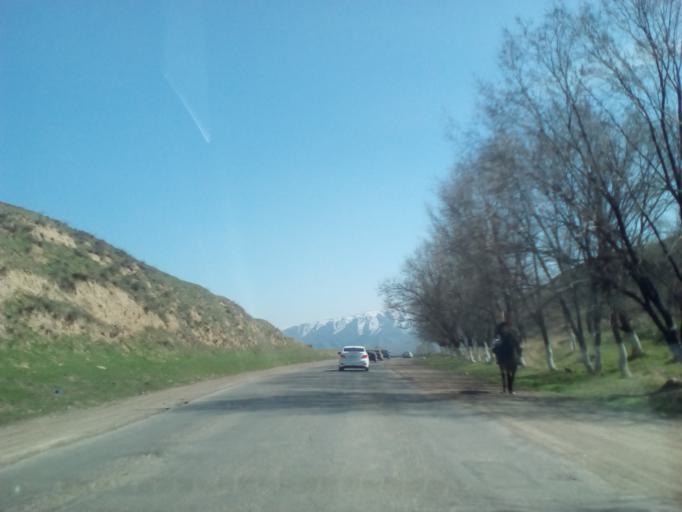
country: KZ
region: Almaty Oblysy
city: Burunday
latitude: 43.1773
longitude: 76.4295
